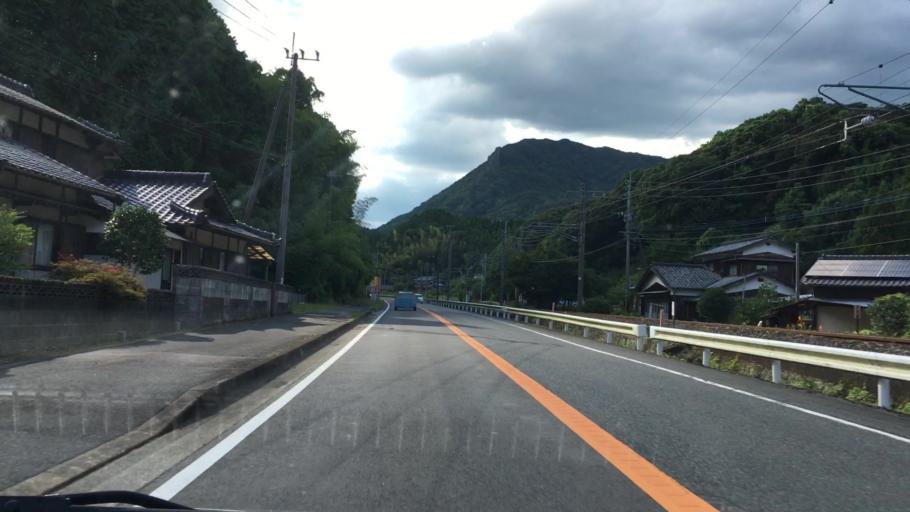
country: JP
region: Saga Prefecture
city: Imaricho-ko
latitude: 33.1910
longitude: 129.9212
